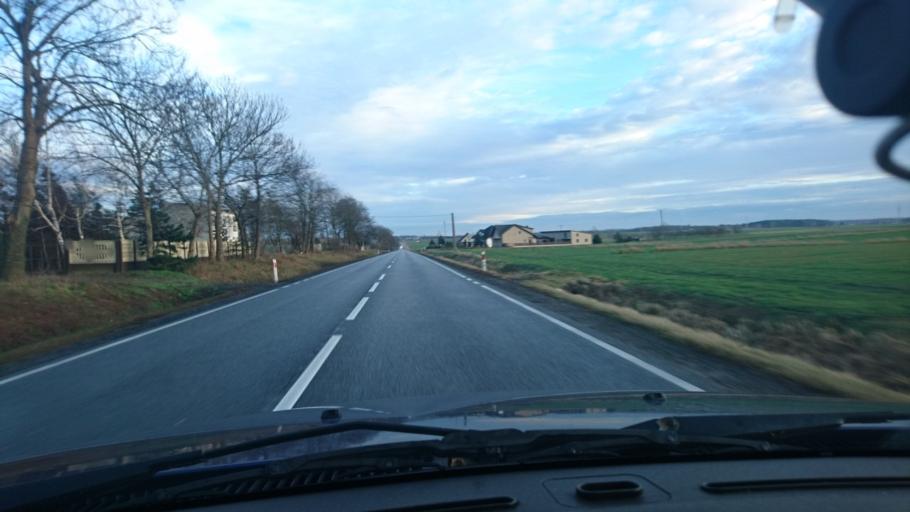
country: PL
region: Greater Poland Voivodeship
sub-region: Powiat kepinski
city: Slupia pod Kepnem
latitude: 51.2375
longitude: 18.0463
